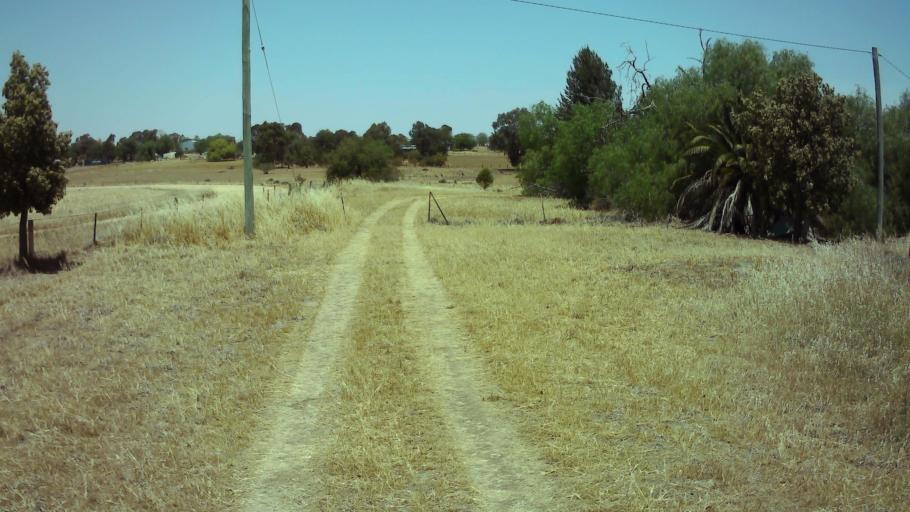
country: AU
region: New South Wales
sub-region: Weddin
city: Grenfell
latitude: -33.8981
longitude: 148.1707
